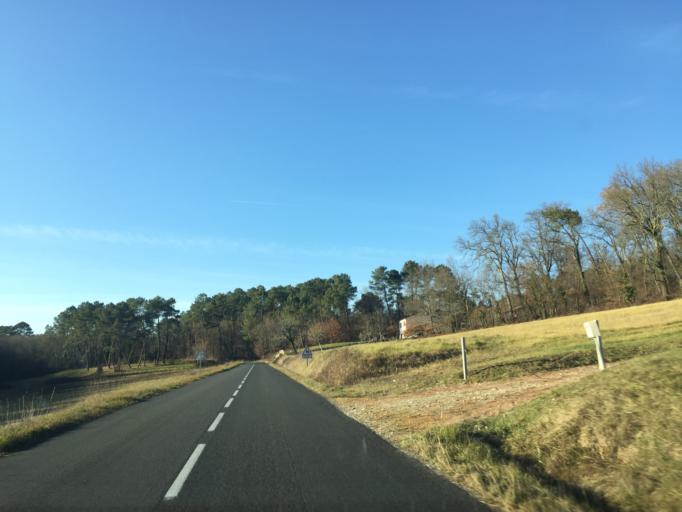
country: FR
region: Aquitaine
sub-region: Departement de la Dordogne
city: Neuvic
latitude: 45.1424
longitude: 0.4423
